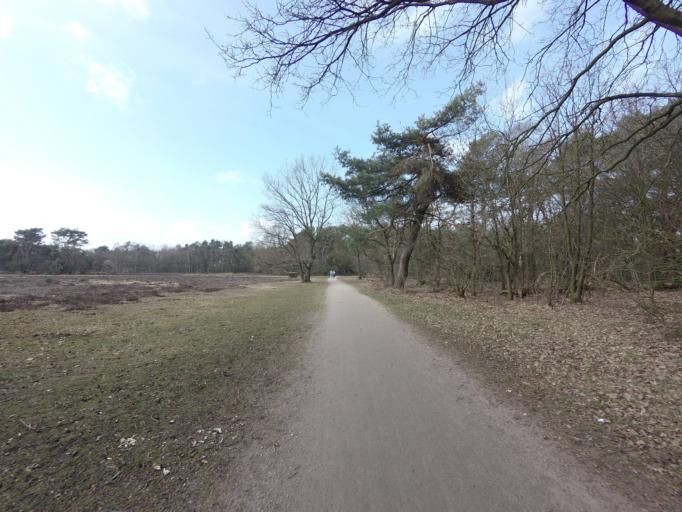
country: NL
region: North Holland
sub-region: Gemeente Bussum
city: Bussum
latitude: 52.2627
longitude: 5.1547
